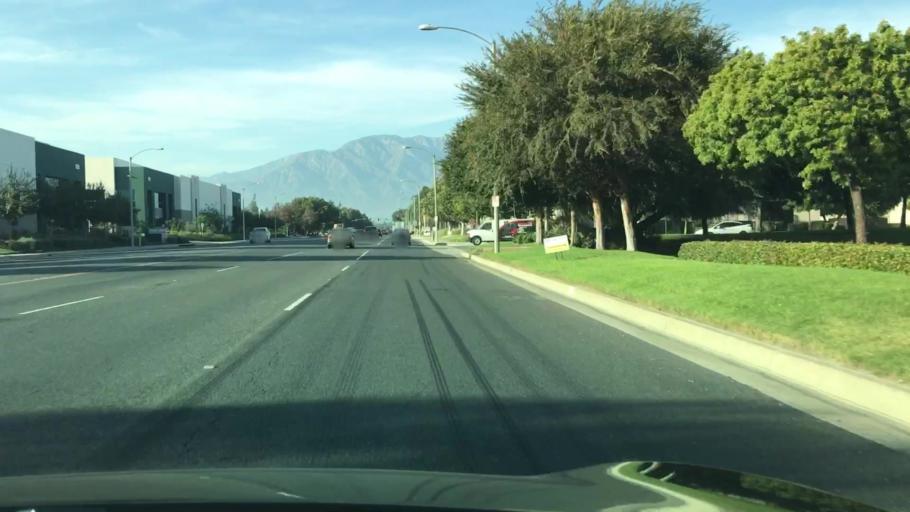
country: US
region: California
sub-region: San Bernardino County
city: Ontario
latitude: 34.0443
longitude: -117.6285
